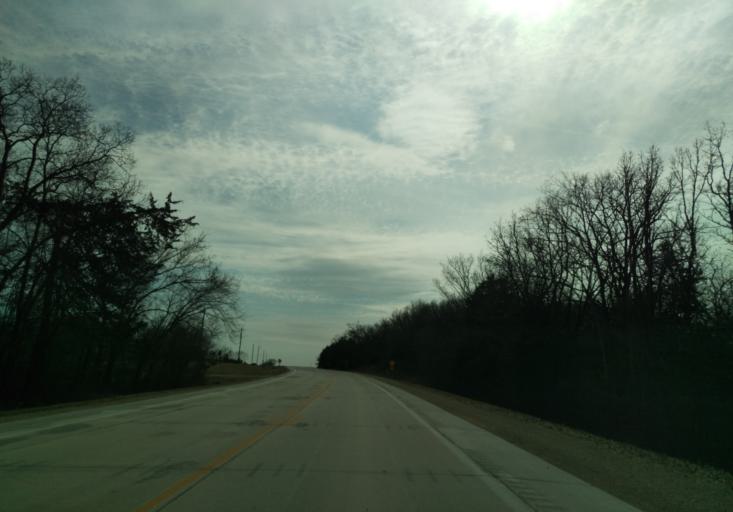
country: US
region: Iowa
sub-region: Winneshiek County
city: Decorah
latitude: 43.3394
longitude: -91.8117
